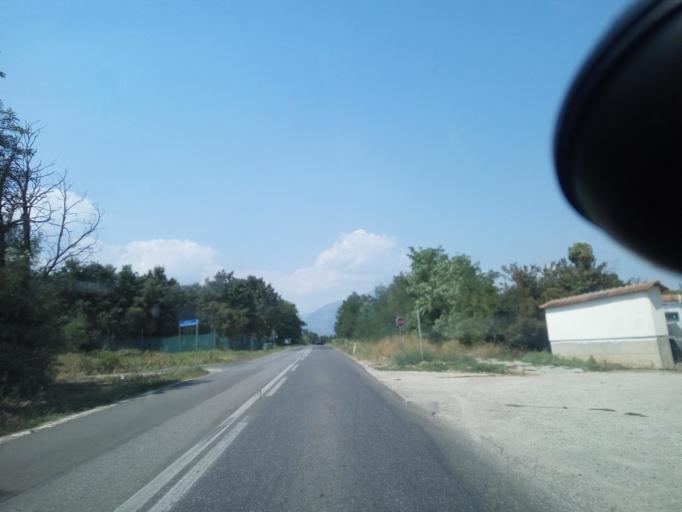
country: XK
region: Gjakova
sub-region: Komuna e Decanit
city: Gllogjan
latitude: 42.4606
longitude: 20.3508
